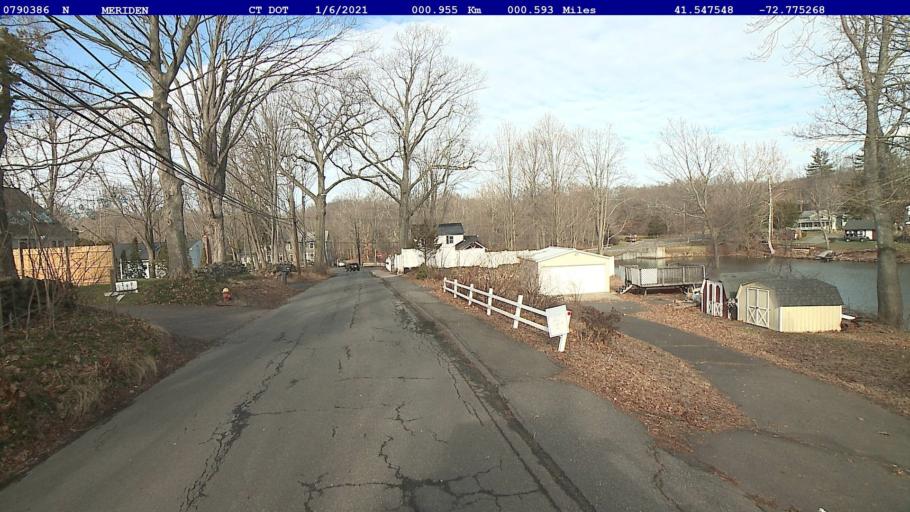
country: US
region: Connecticut
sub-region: New Haven County
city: Meriden
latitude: 41.5476
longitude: -72.7753
